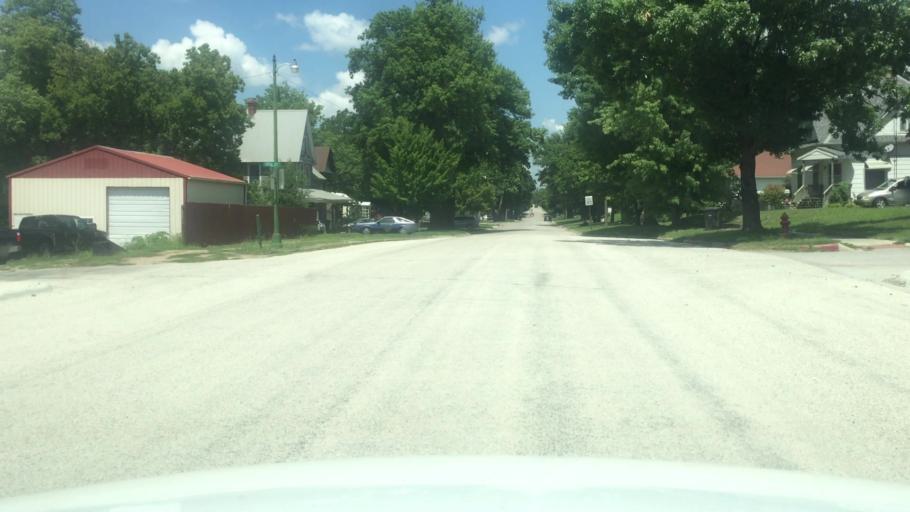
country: US
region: Kansas
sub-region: Brown County
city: Horton
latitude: 39.6619
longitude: -95.5273
